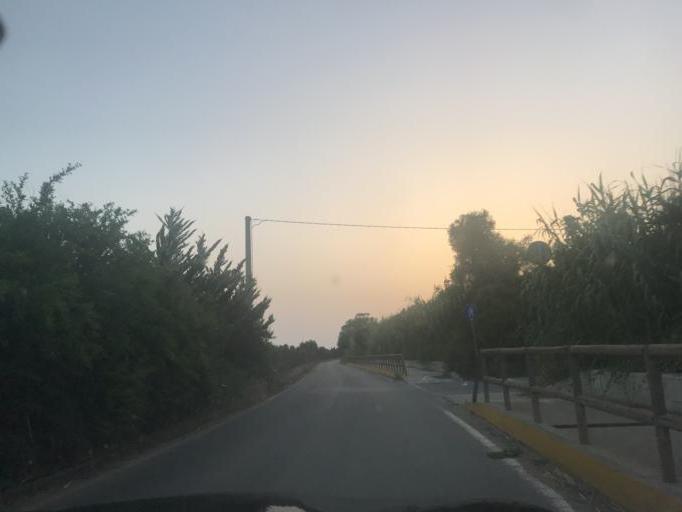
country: IT
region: Sardinia
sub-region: Provincia di Sassari
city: Alghero
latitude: 40.5512
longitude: 8.3435
